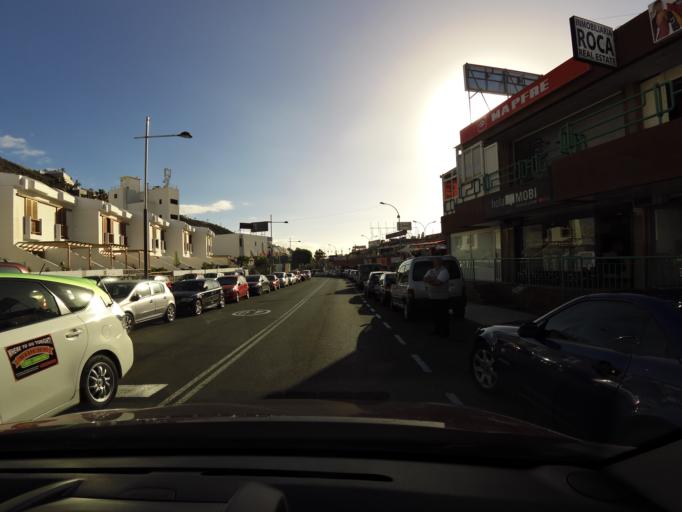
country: ES
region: Canary Islands
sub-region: Provincia de Las Palmas
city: Puerto Rico
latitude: 27.7927
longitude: -15.7072
